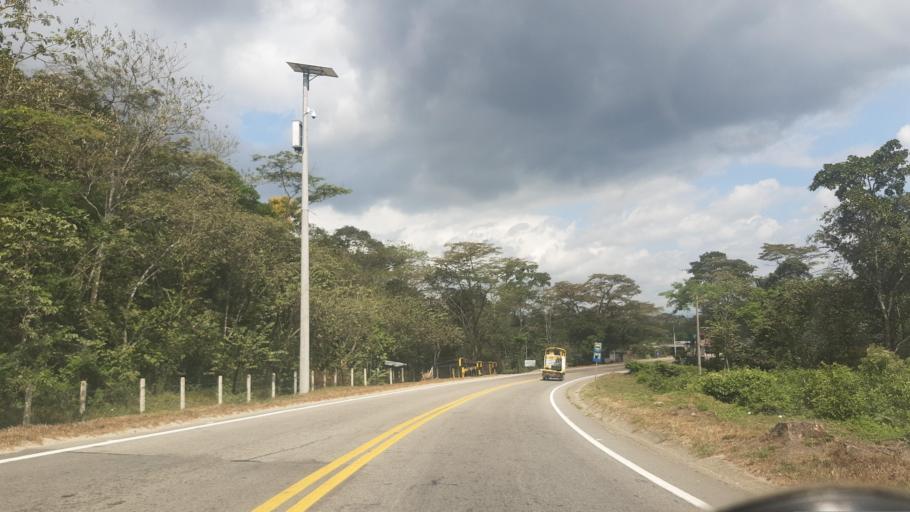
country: CO
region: Casanare
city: Tauramena
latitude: 5.0059
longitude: -72.6899
